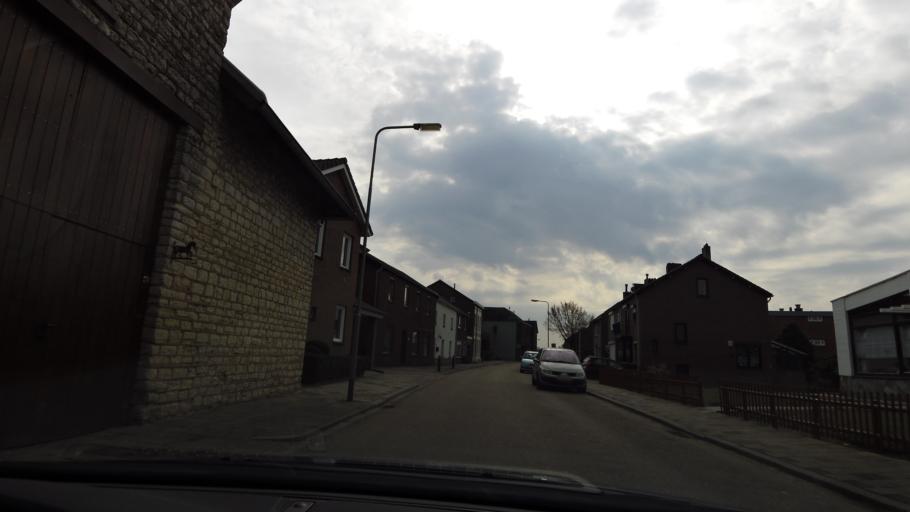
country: NL
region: Limburg
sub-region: Gemeente Simpelveld
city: Simpelveld
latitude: 50.8222
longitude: 6.0084
